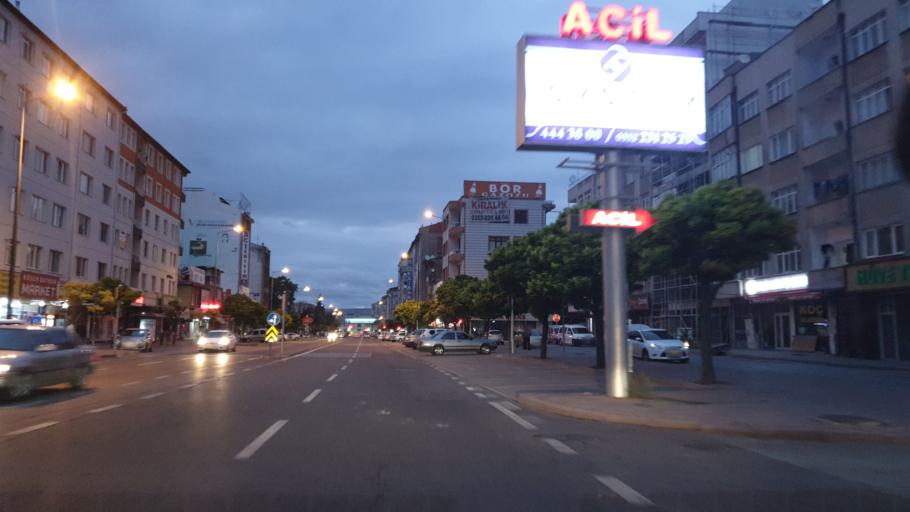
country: TR
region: Kayseri
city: Kayseri
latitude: 38.7251
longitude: 35.4807
